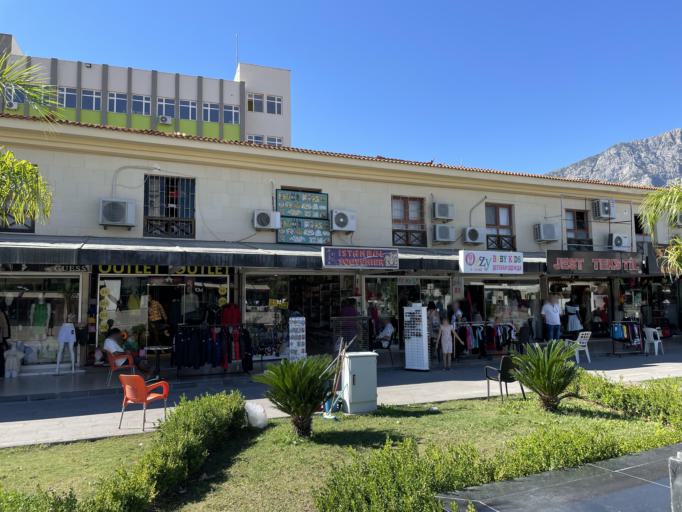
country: TR
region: Antalya
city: Kemer
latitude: 36.6018
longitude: 30.5590
